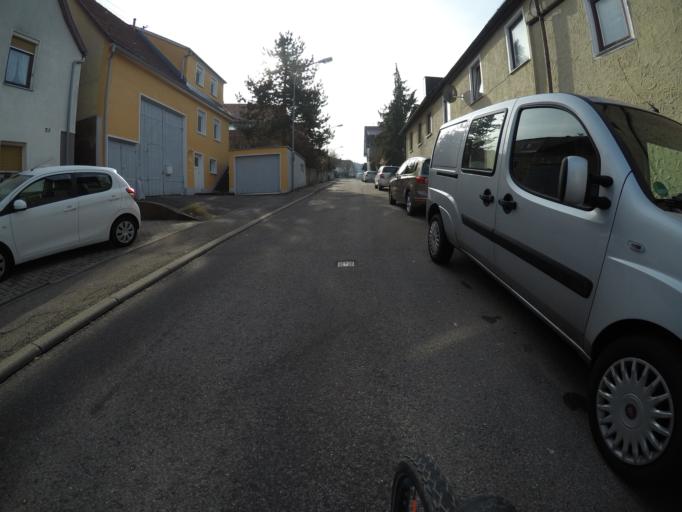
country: DE
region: Baden-Wuerttemberg
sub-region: Karlsruhe Region
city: Calw
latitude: 48.6928
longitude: 8.7710
